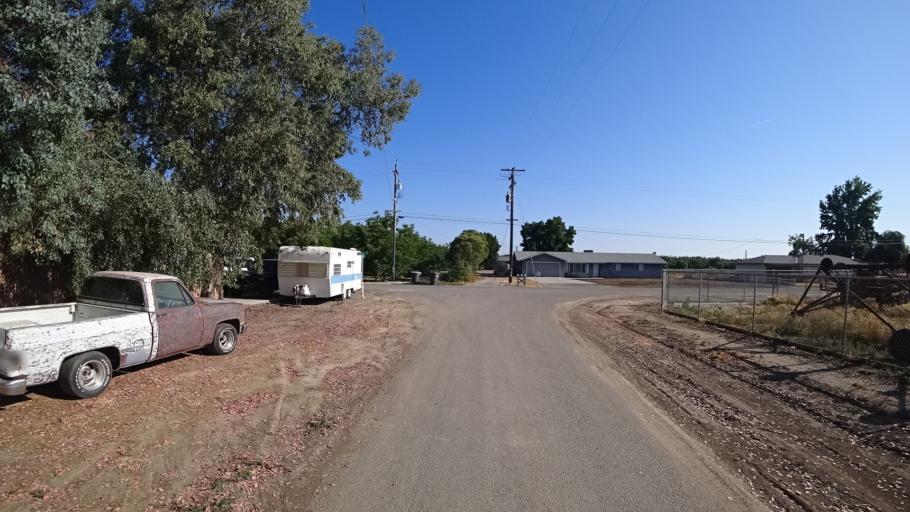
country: US
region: California
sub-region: Fresno County
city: Laton
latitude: 36.4029
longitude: -119.7198
